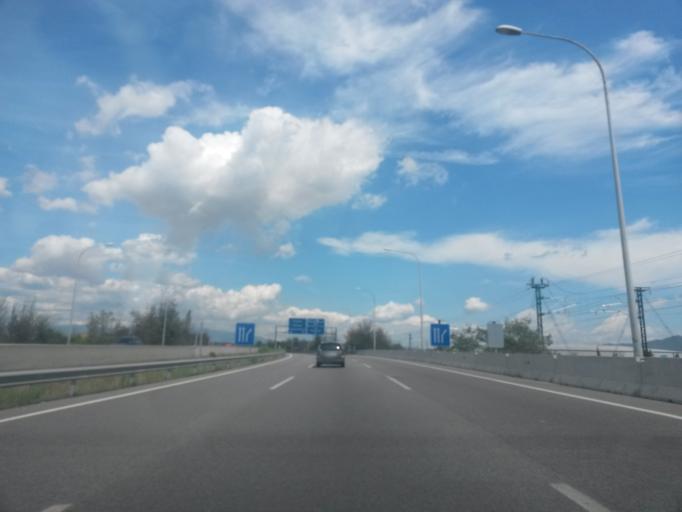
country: ES
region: Catalonia
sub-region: Provincia de Barcelona
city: Montmelo
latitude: 41.5440
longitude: 2.2318
